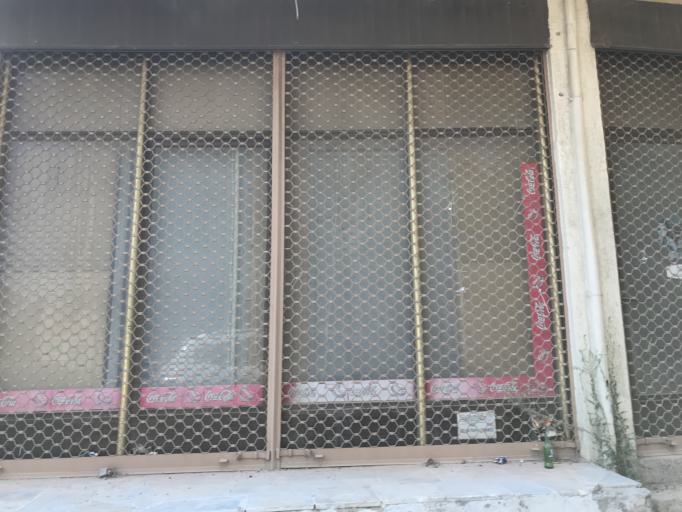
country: TR
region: Izmir
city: Karabaglar
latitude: 38.3877
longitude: 27.1309
